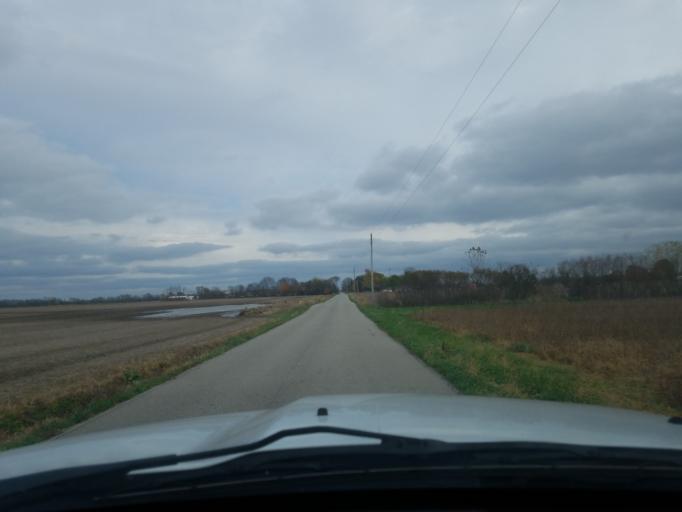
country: US
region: Indiana
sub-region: Shelby County
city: Shelbyville
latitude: 39.5545
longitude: -85.8458
